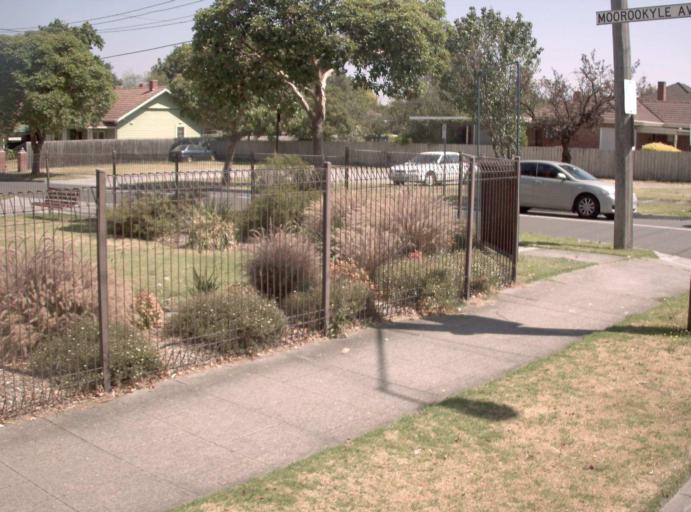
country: AU
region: Victoria
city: Hughesdale
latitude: -37.9077
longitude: 145.0854
